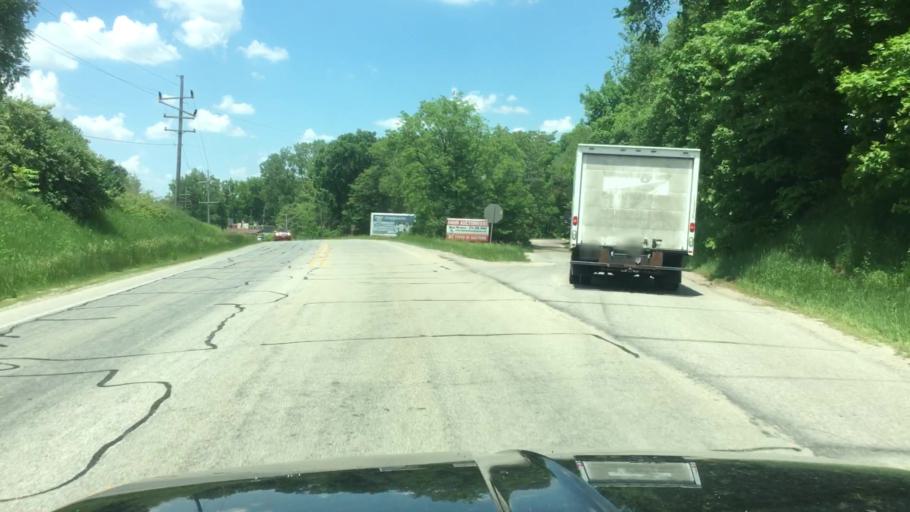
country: US
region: Indiana
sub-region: Kosciusko County
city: North Webster
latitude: 41.3143
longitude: -85.6912
